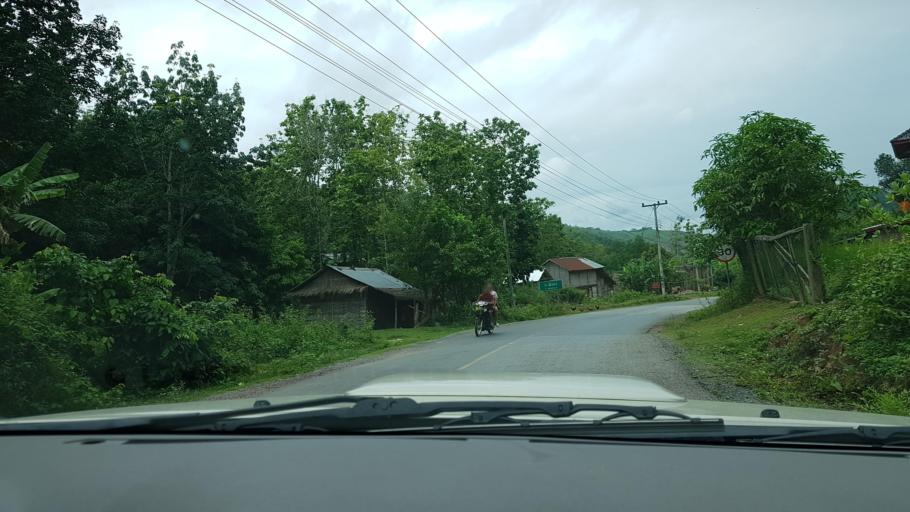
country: LA
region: Loungnamtha
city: Muang Nale
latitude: 20.3606
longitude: 101.7119
